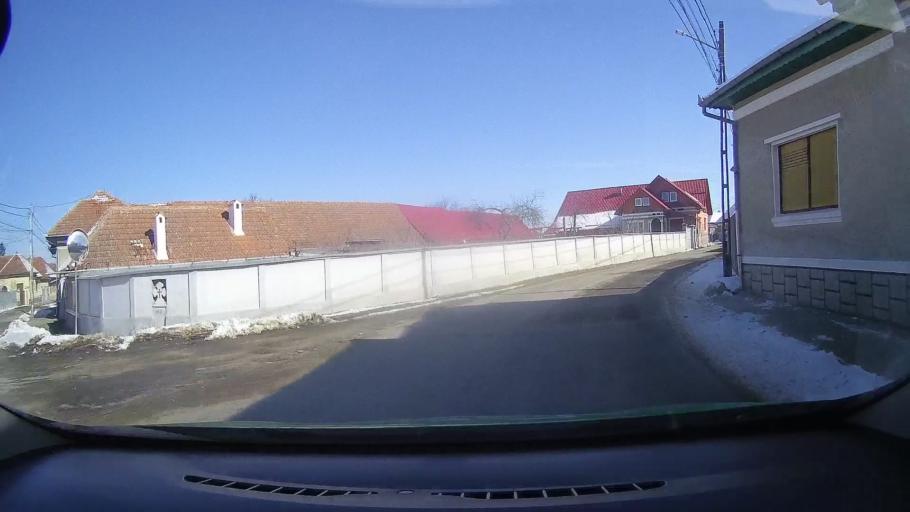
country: RO
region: Brasov
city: Ucea de Sus
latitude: 45.7524
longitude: 24.6813
